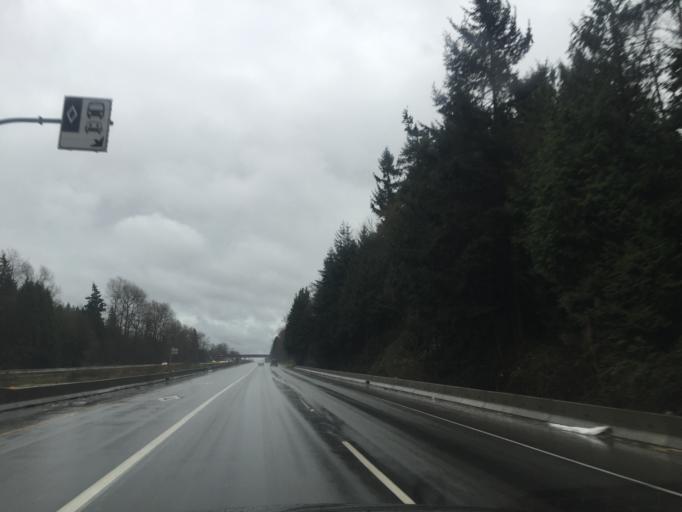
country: CA
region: British Columbia
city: Walnut Grove
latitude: 49.1606
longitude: -122.6564
